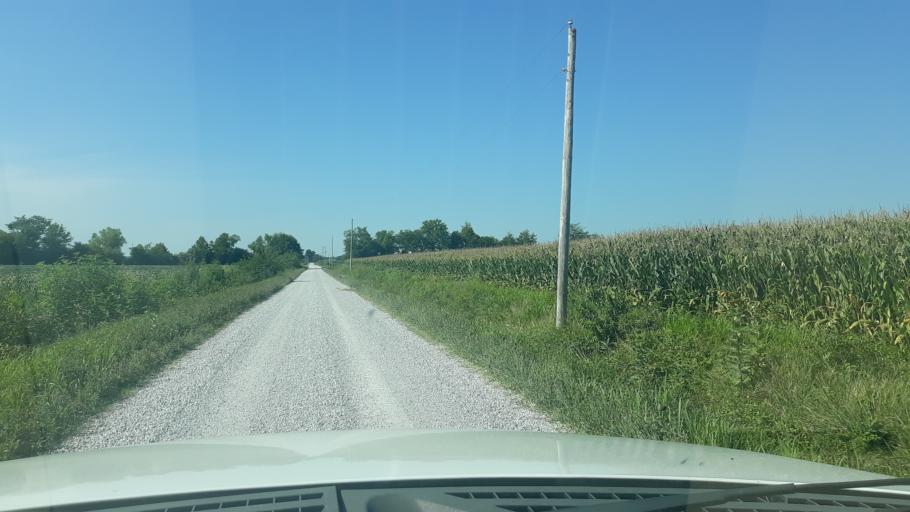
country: US
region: Illinois
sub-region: Saline County
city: Eldorado
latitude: 37.8489
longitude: -88.4849
